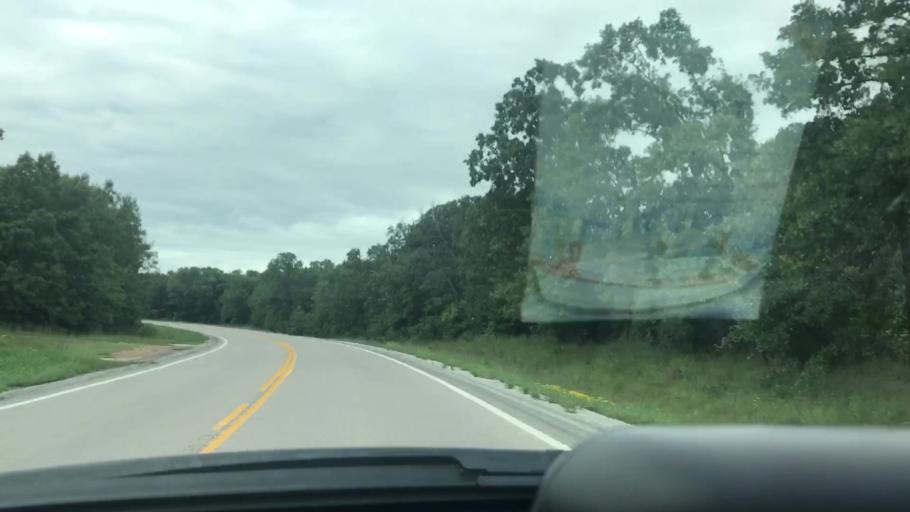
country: US
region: Missouri
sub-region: Benton County
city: Warsaw
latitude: 38.1590
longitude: -93.2974
